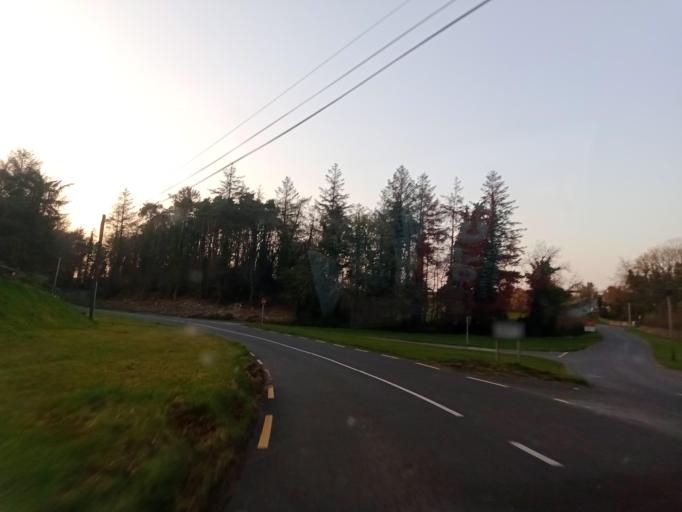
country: IE
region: Leinster
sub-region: Laois
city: Abbeyleix
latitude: 52.8879
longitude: -7.3090
